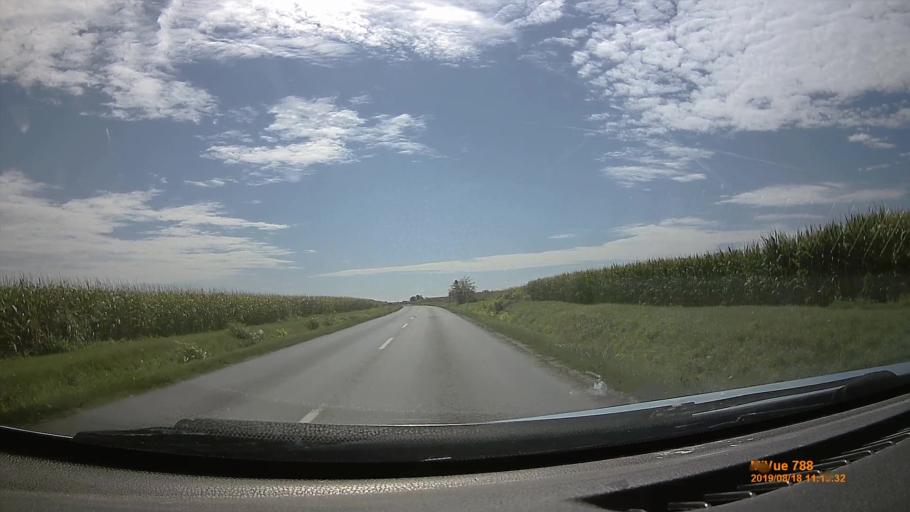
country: HU
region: Fejer
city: Szabadbattyan
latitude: 47.0998
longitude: 18.3879
